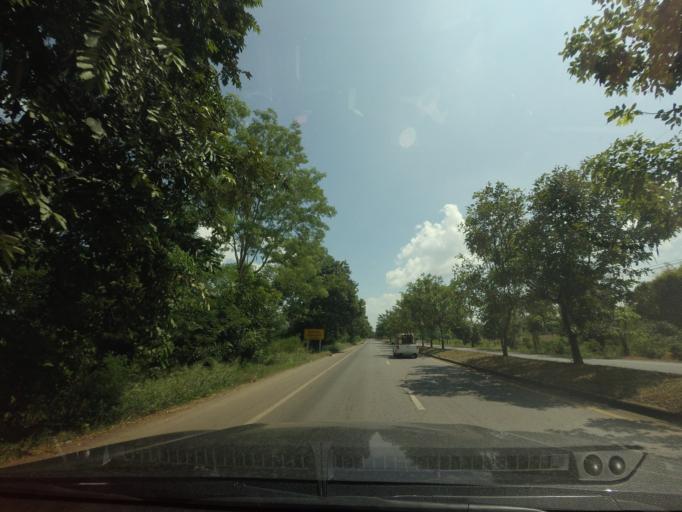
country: TH
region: Phetchabun
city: Nong Phai
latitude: 16.0513
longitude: 101.0784
